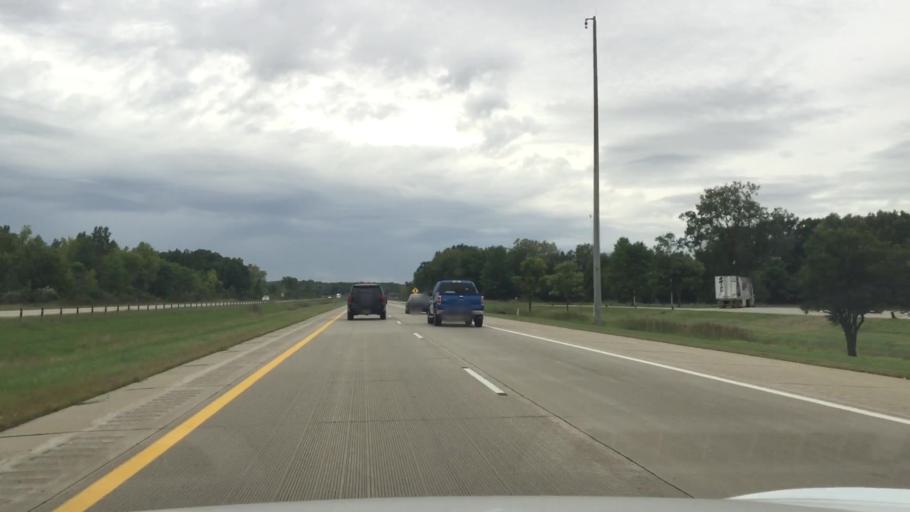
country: US
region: Michigan
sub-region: Macomb County
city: New Baltimore
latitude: 42.7429
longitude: -82.7190
